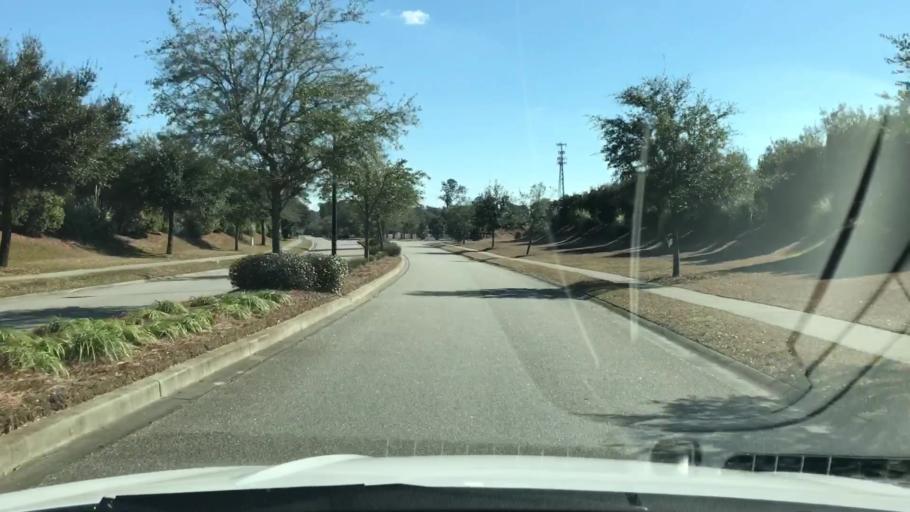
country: US
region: South Carolina
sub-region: Horry County
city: Socastee
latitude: 33.6437
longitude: -79.0361
